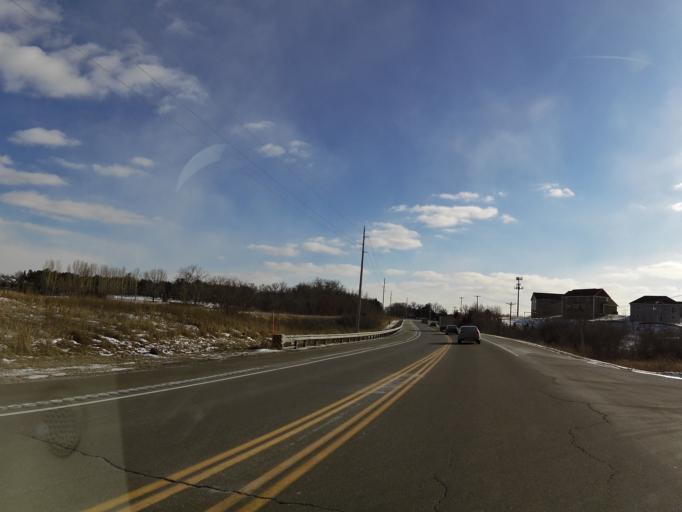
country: US
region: Minnesota
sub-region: Dakota County
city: Rosemount
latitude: 44.7795
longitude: -93.1166
